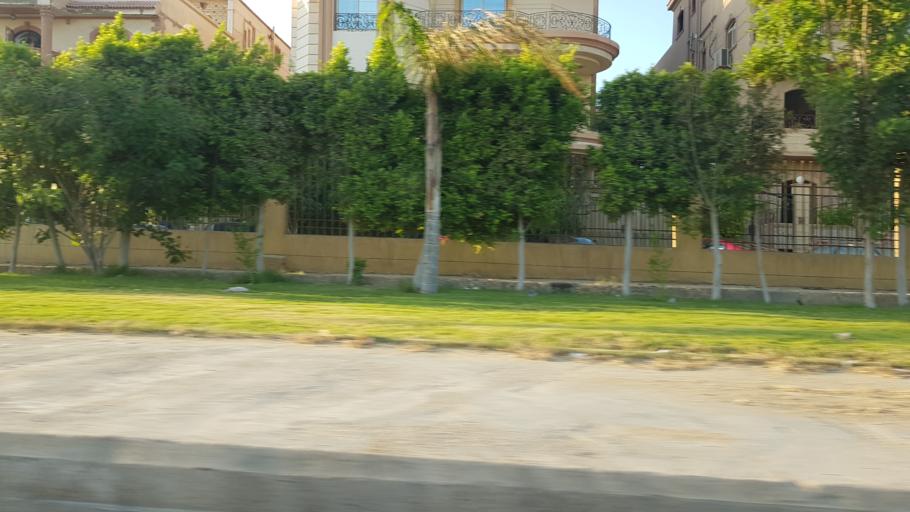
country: EG
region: Muhafazat al Qalyubiyah
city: Al Khankah
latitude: 30.0612
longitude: 31.4430
